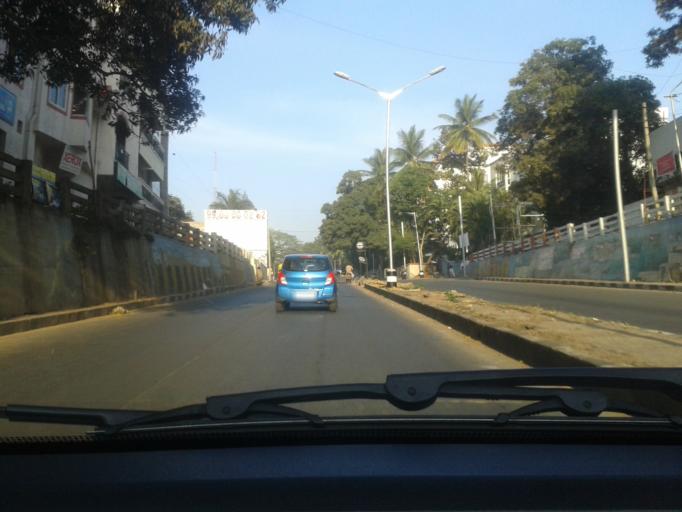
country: IN
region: Karnataka
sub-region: Bangalore Urban
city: Bangalore
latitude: 12.9946
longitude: 77.6046
